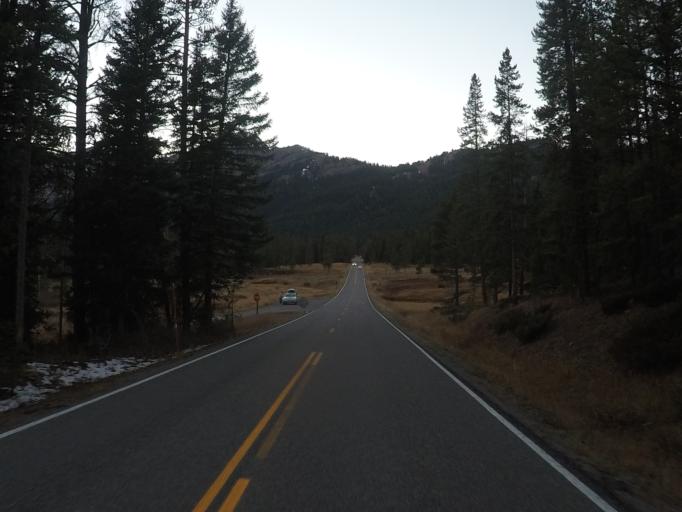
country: US
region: Montana
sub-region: Stillwater County
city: Absarokee
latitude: 45.0043
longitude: -110.0305
